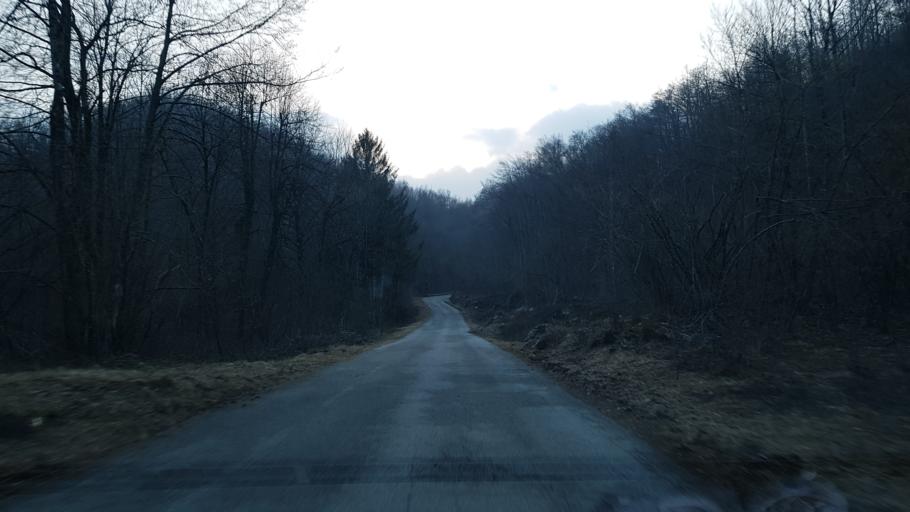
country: IT
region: Friuli Venezia Giulia
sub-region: Provincia di Udine
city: Taipana
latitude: 46.2168
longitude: 13.3942
